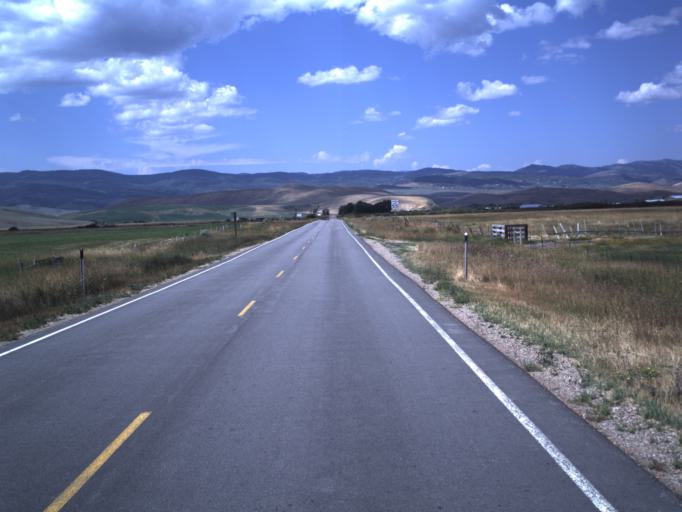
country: US
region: Utah
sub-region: Rich County
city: Randolph
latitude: 41.8328
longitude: -111.3255
